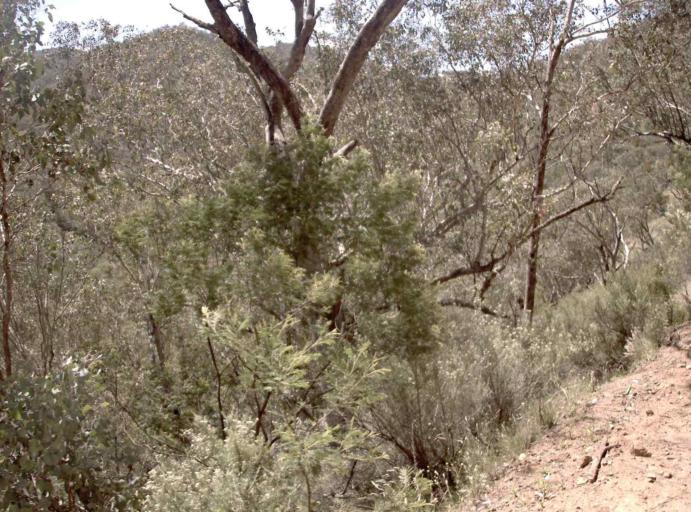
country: AU
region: New South Wales
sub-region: Snowy River
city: Jindabyne
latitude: -37.0470
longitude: 148.5402
